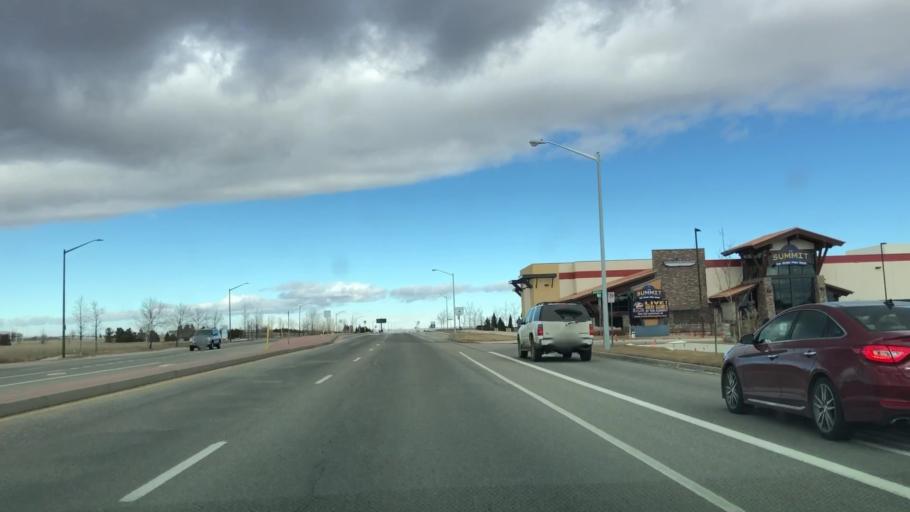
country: US
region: Colorado
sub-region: Weld County
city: Windsor
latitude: 40.4373
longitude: -104.9824
